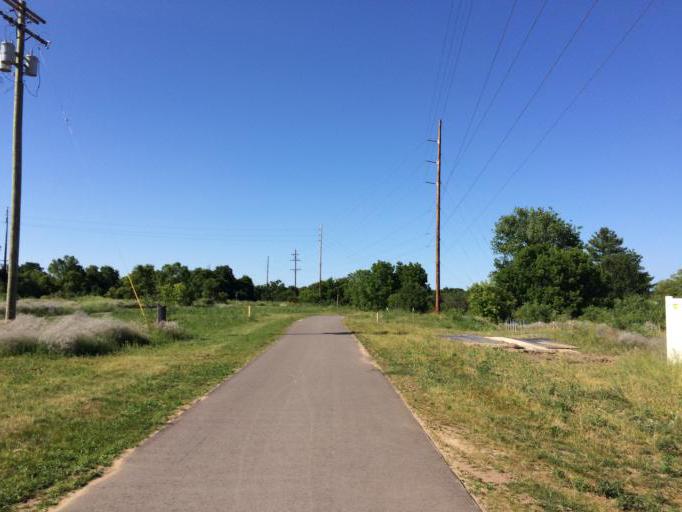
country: US
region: Michigan
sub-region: Grand Traverse County
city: Traverse City
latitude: 44.7541
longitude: -85.6168
